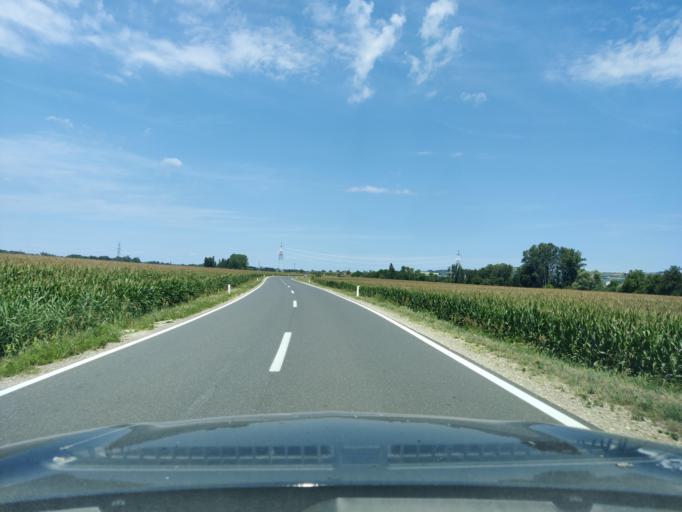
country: SI
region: Lendava-Lendva
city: Lendava
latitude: 46.5284
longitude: 16.4422
